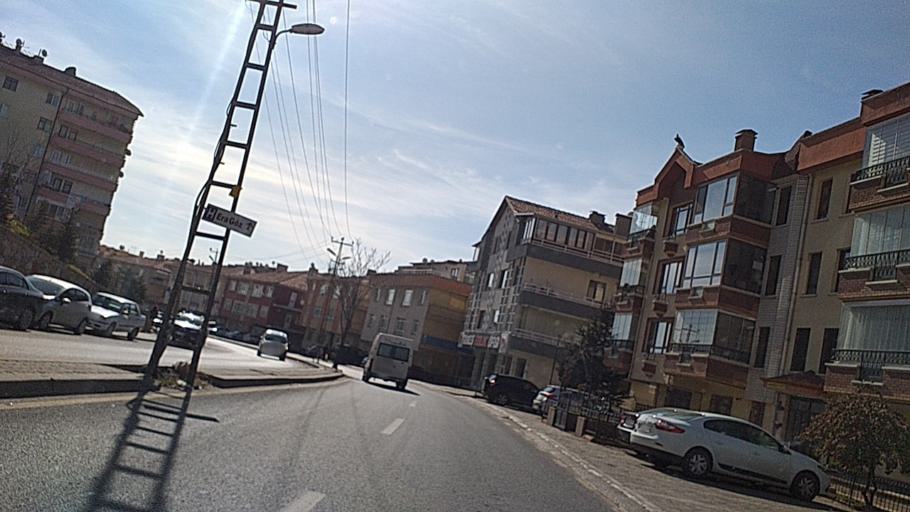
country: TR
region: Ankara
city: Ankara
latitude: 39.9851
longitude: 32.8235
